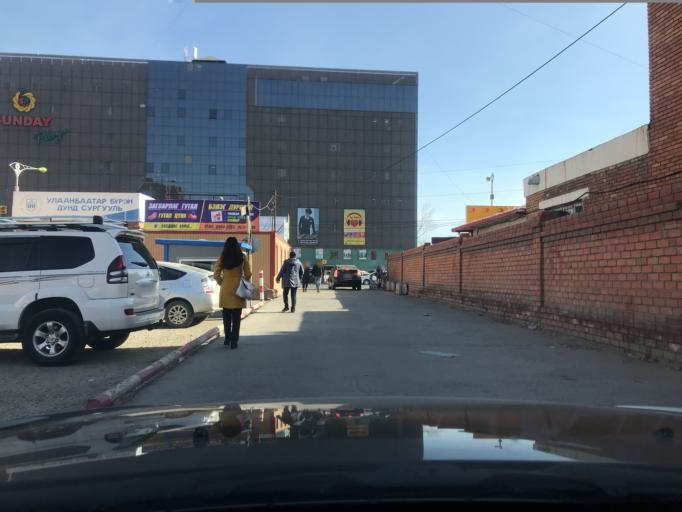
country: MN
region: Ulaanbaatar
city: Ulaanbaatar
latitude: 47.9110
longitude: 106.9429
